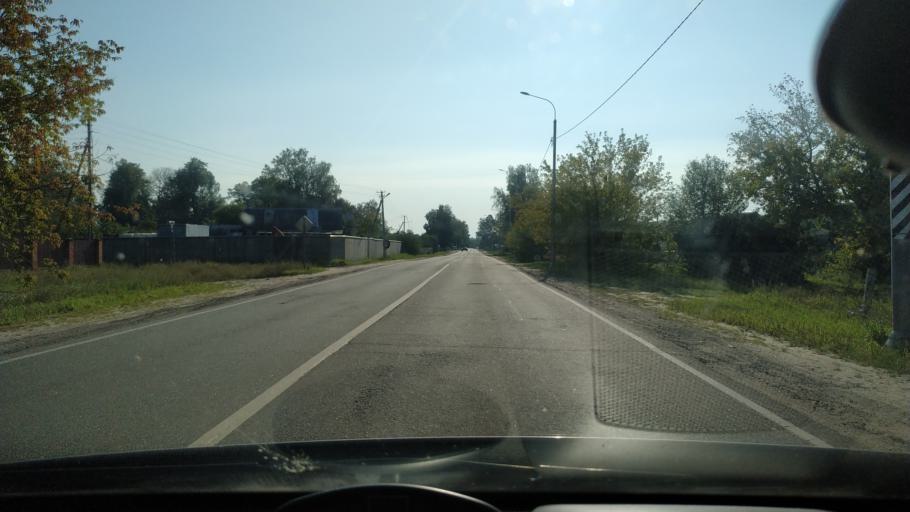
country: RU
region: Moskovskaya
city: Kerva
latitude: 55.5625
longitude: 39.6663
